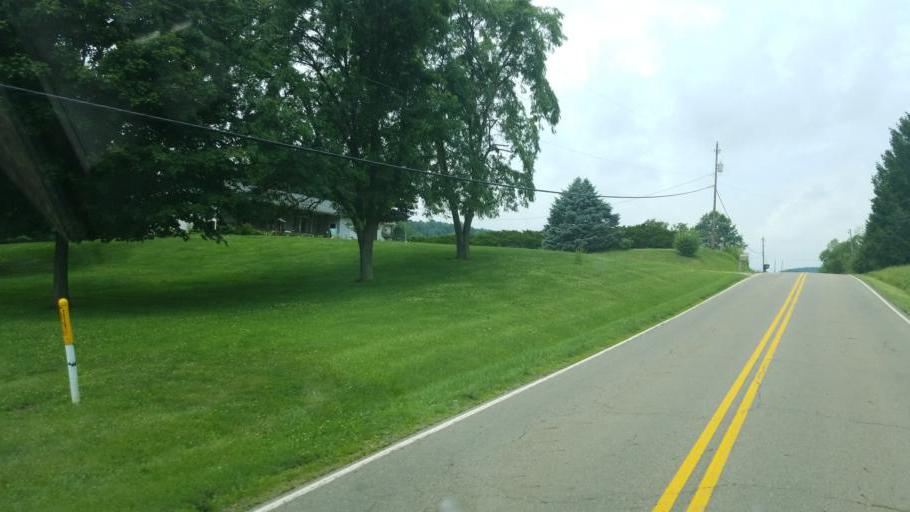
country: US
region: Ohio
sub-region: Licking County
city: Newark
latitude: 40.1291
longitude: -82.4502
